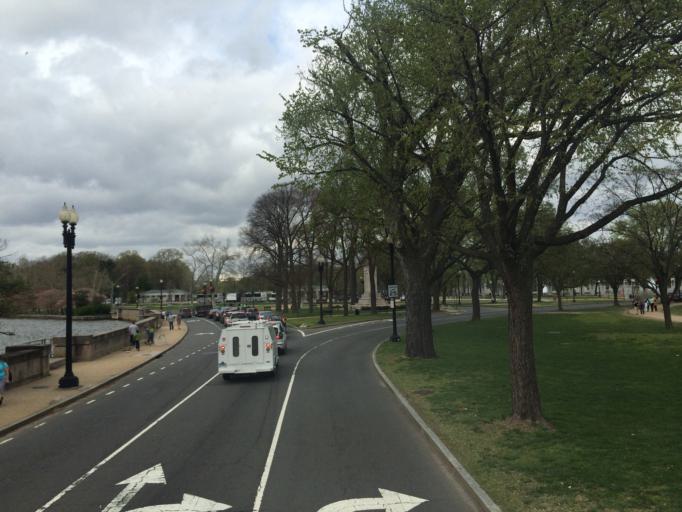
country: US
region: Washington, D.C.
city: Washington, D.C.
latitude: 38.8879
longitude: -77.0383
